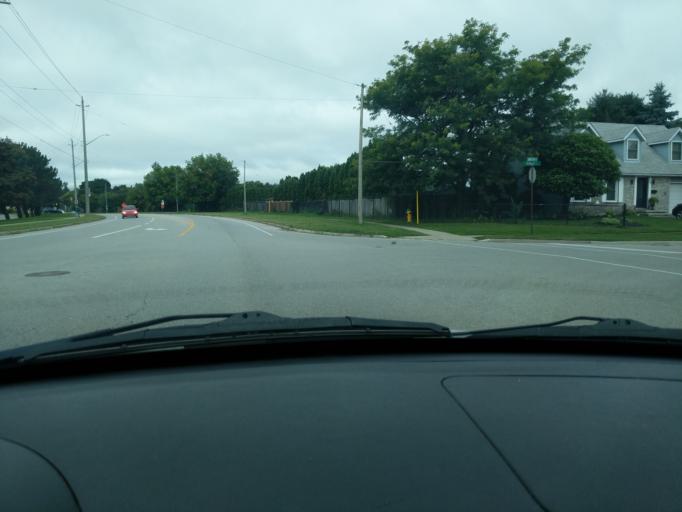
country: CA
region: Ontario
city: Cambridge
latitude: 43.4181
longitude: -80.3078
